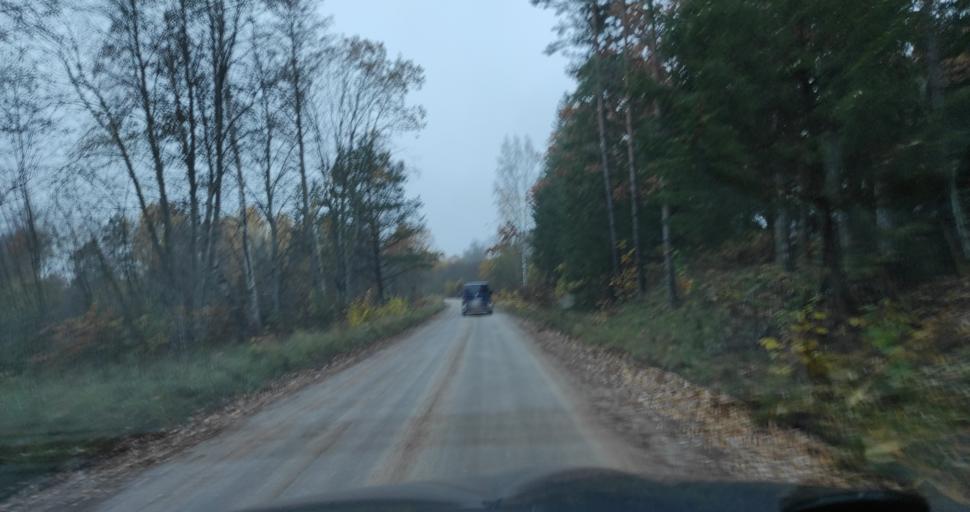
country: LV
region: Pavilostas
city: Pavilosta
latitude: 56.7608
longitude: 21.2734
